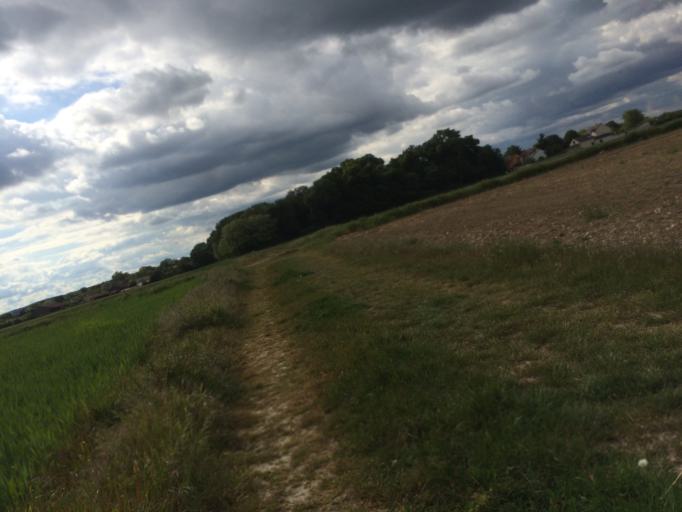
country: FR
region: Ile-de-France
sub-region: Departement de l'Essonne
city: Le Plessis-Pate
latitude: 48.6166
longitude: 2.3155
